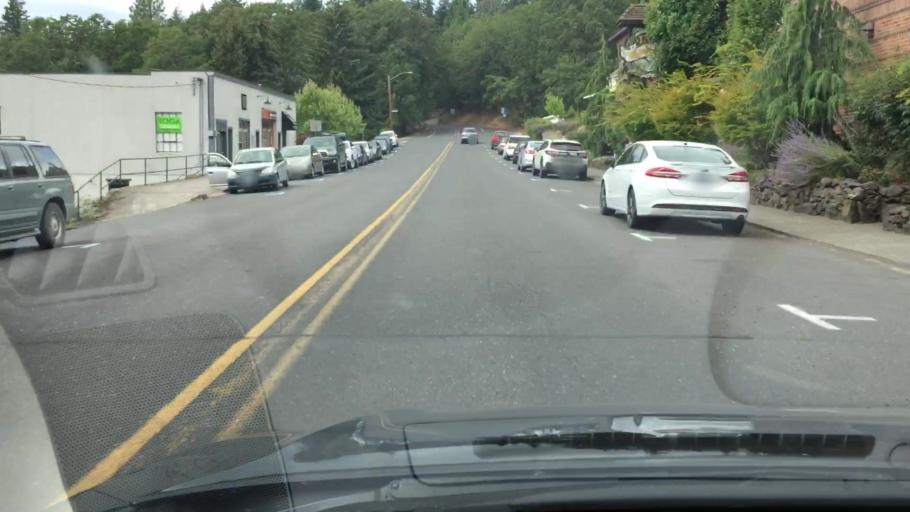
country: US
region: Washington
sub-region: Klickitat County
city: White Salmon
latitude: 45.7278
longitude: -121.4879
